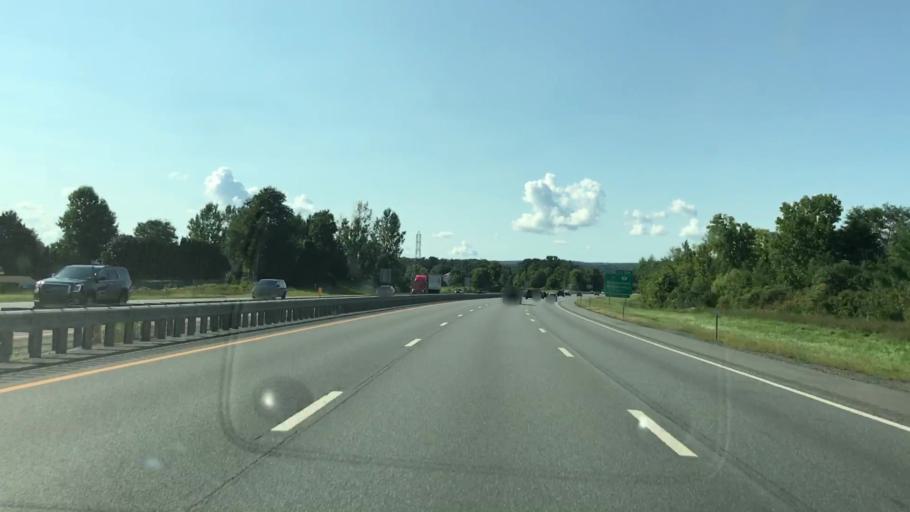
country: US
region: New York
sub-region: Schenectady County
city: Rotterdam
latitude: 42.7761
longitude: -73.9942
